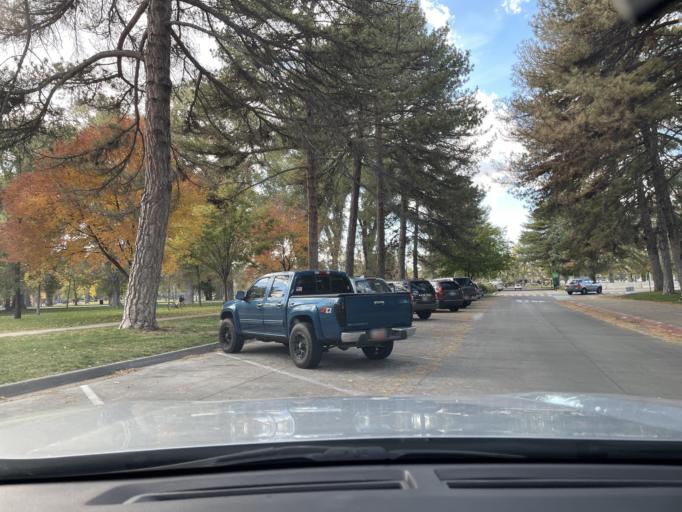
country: US
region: Utah
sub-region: Salt Lake County
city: Salt Lake City
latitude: 40.7491
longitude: -111.8730
